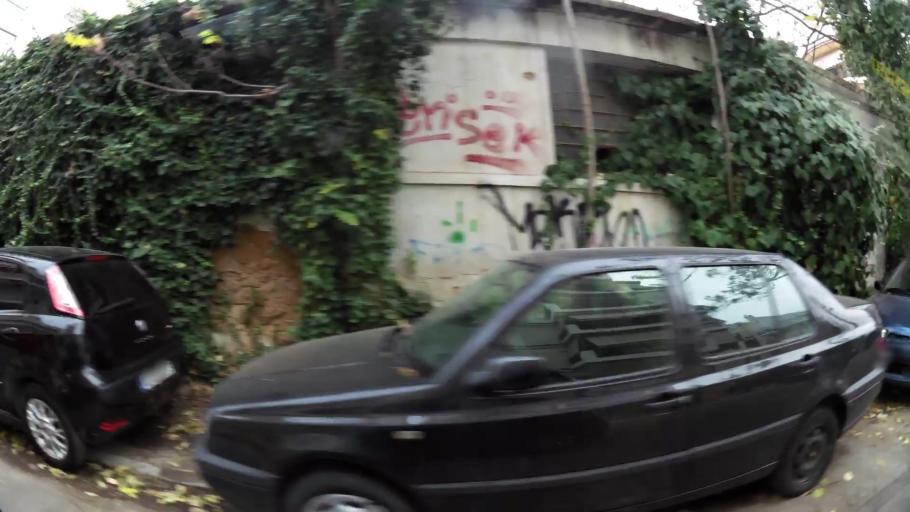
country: GR
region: Attica
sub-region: Nomarchia Athinas
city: Nea Ionia
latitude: 38.0391
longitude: 23.7704
